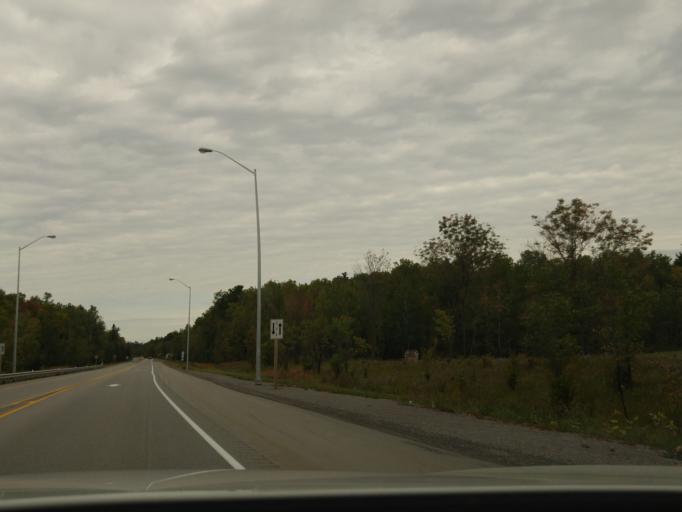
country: CA
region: Ontario
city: Arnprior
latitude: 45.4401
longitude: -76.4651
